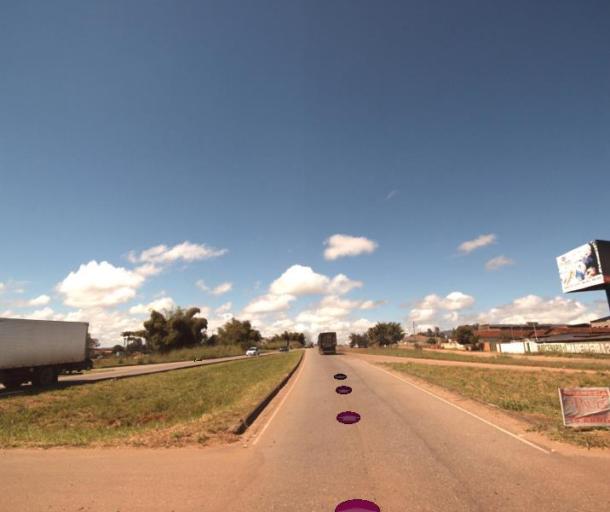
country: BR
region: Goias
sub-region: Jaragua
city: Jaragua
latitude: -15.7357
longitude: -49.3232
